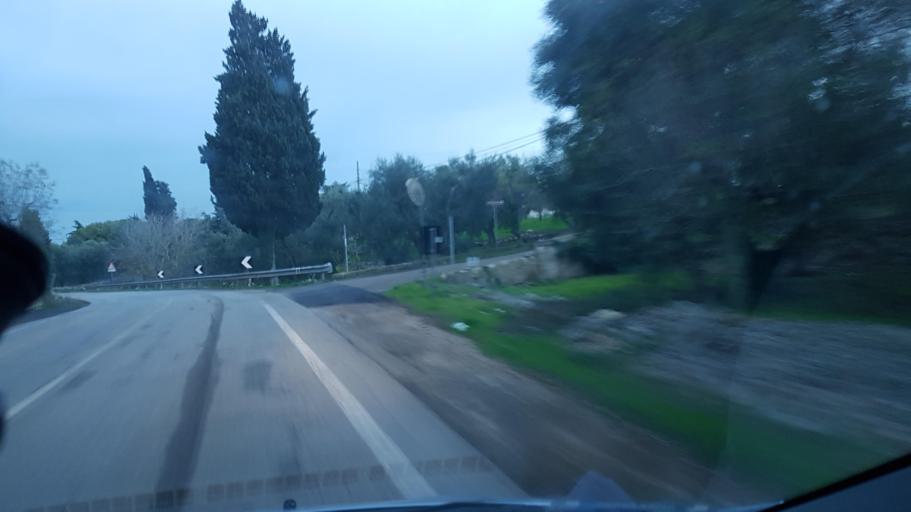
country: IT
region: Apulia
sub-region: Provincia di Brindisi
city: San Michele Salentino
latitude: 40.6422
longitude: 17.5766
